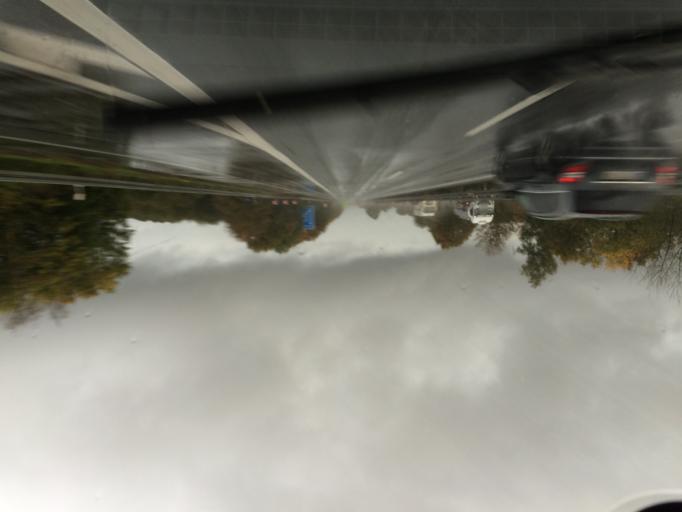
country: DE
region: North Rhine-Westphalia
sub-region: Regierungsbezirk Munster
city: Haltern
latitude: 51.7728
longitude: 7.1763
